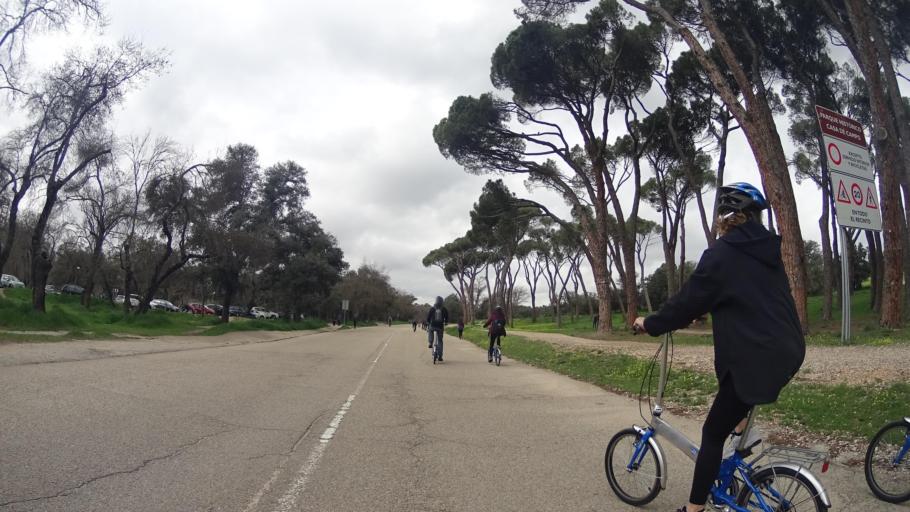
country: ES
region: Madrid
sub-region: Provincia de Madrid
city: Moncloa-Aravaca
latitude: 40.4160
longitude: -3.7477
